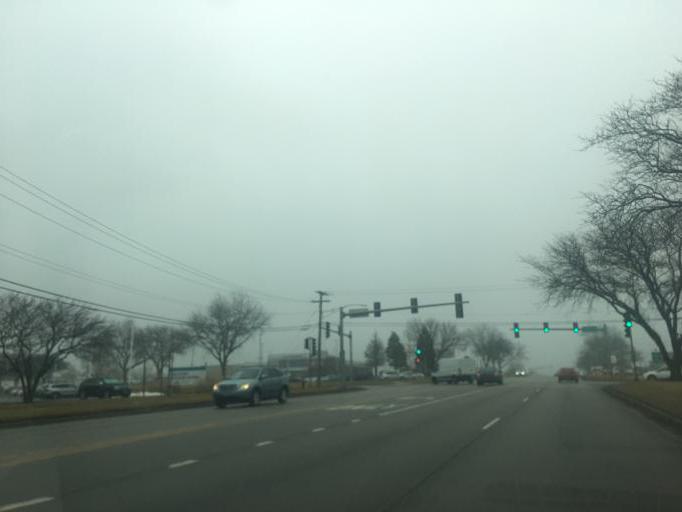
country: US
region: Illinois
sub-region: DuPage County
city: Lisle
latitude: 41.7983
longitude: -88.0976
